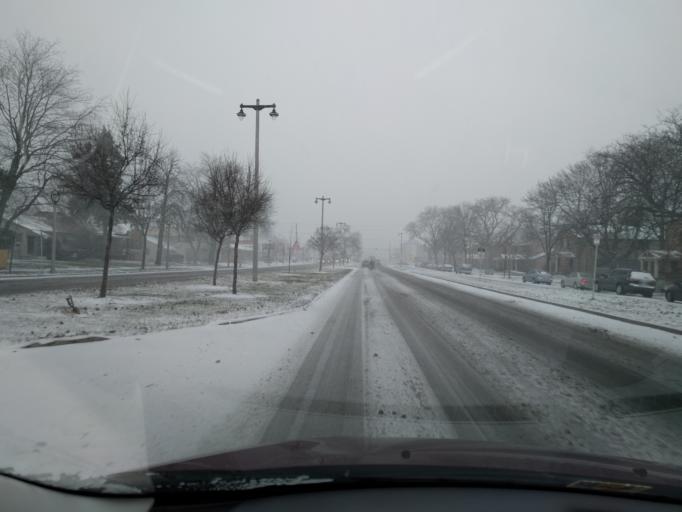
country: US
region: Wisconsin
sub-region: Milwaukee County
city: Brown Deer
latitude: 43.1194
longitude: -87.9936
